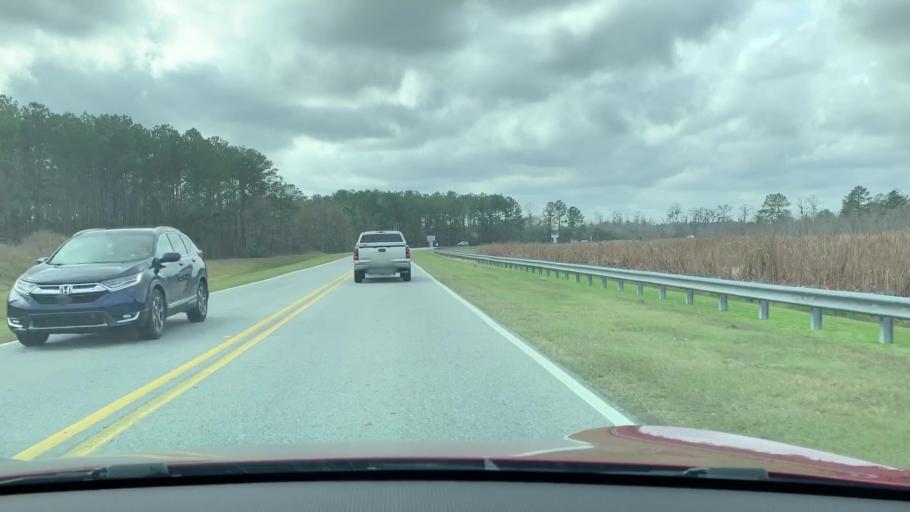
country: US
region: Georgia
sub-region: Chatham County
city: Pooler
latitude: 32.1404
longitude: -81.2121
